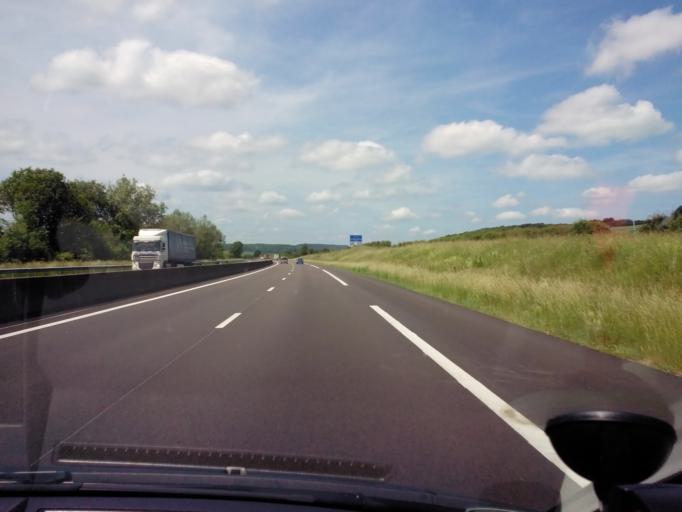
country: FR
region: Champagne-Ardenne
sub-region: Departement de la Haute-Marne
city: Rolampont
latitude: 47.9487
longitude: 5.3225
